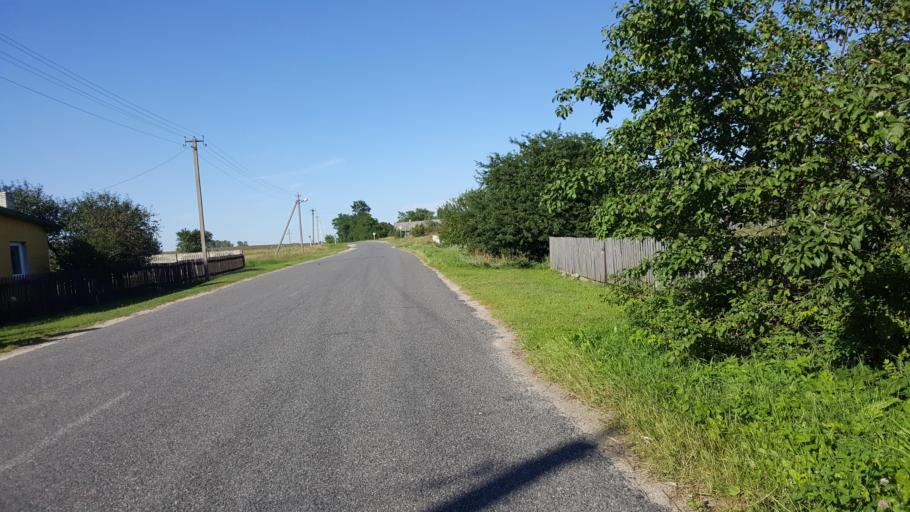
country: BY
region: Brest
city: Kamyanyets
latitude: 52.3829
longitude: 23.7446
